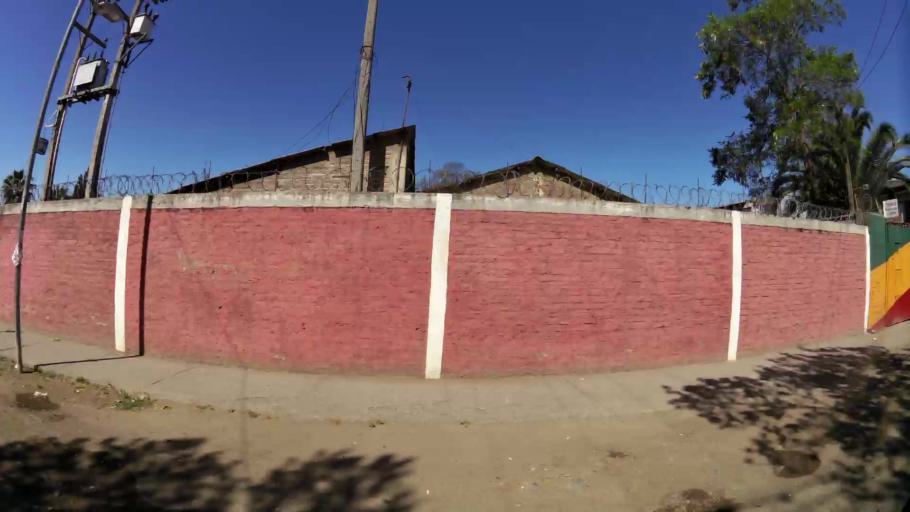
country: CL
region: Santiago Metropolitan
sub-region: Provincia de Maipo
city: San Bernardo
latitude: -33.5928
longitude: -70.7097
